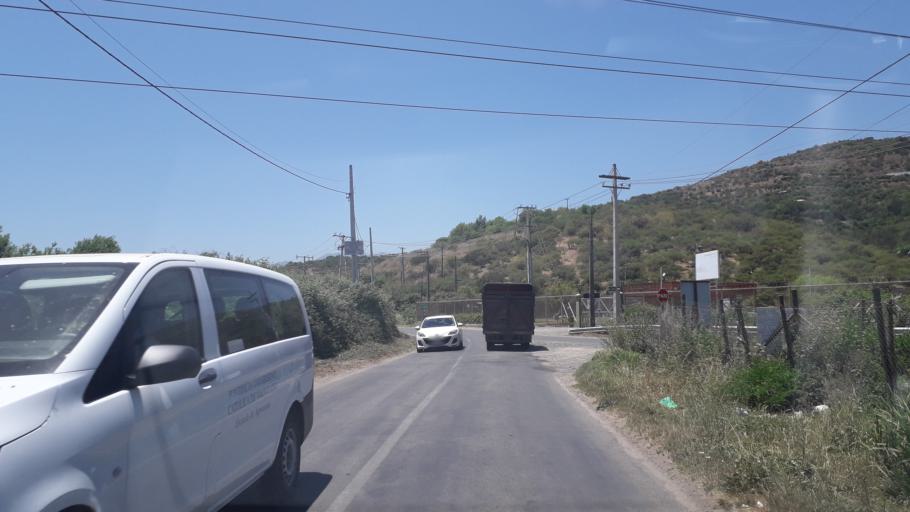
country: CL
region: Valparaiso
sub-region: Provincia de Quillota
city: Quillota
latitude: -32.9353
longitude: -71.2658
